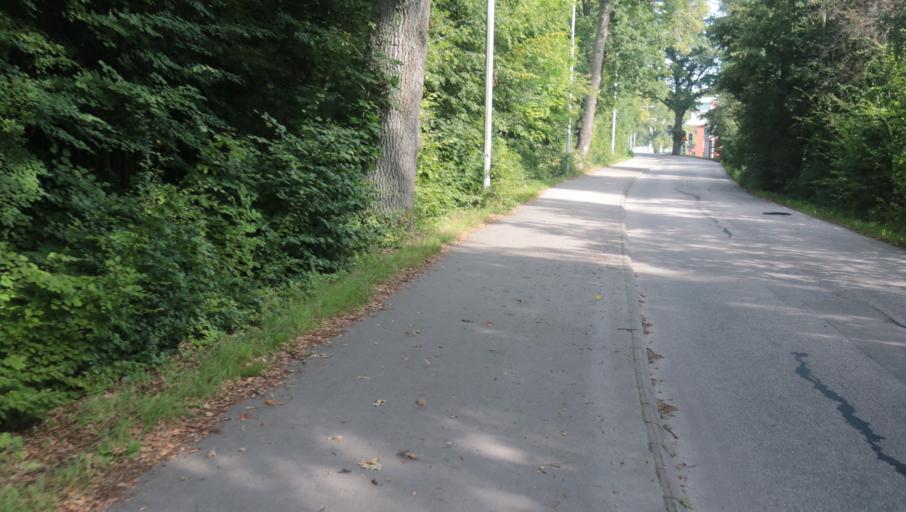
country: SE
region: Blekinge
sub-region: Karlshamns Kommun
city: Karlshamn
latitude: 56.1913
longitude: 14.8511
